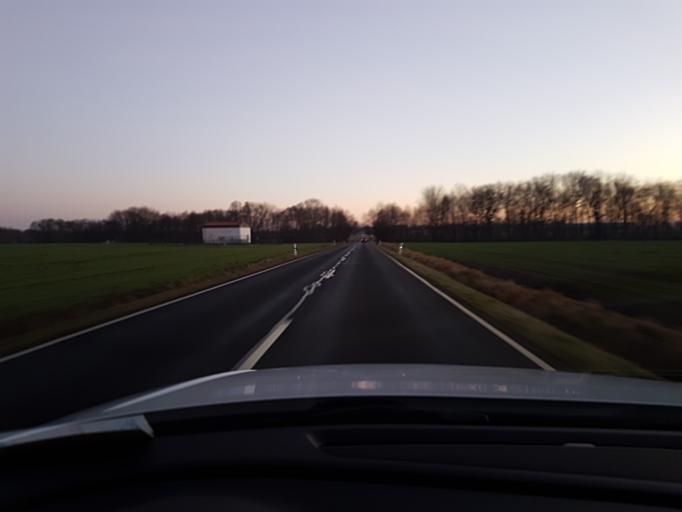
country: DE
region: Mecklenburg-Vorpommern
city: Gingst
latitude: 54.4748
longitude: 13.2936
